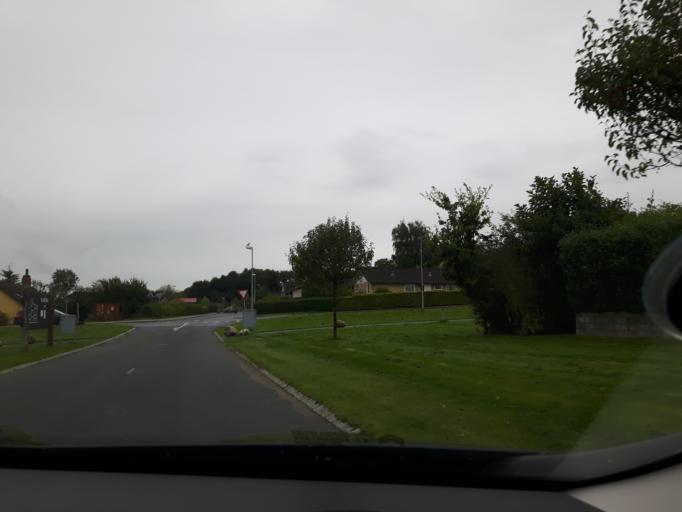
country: DK
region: Central Jutland
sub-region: Skanderborg Kommune
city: Ry
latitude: 56.1541
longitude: 9.8027
